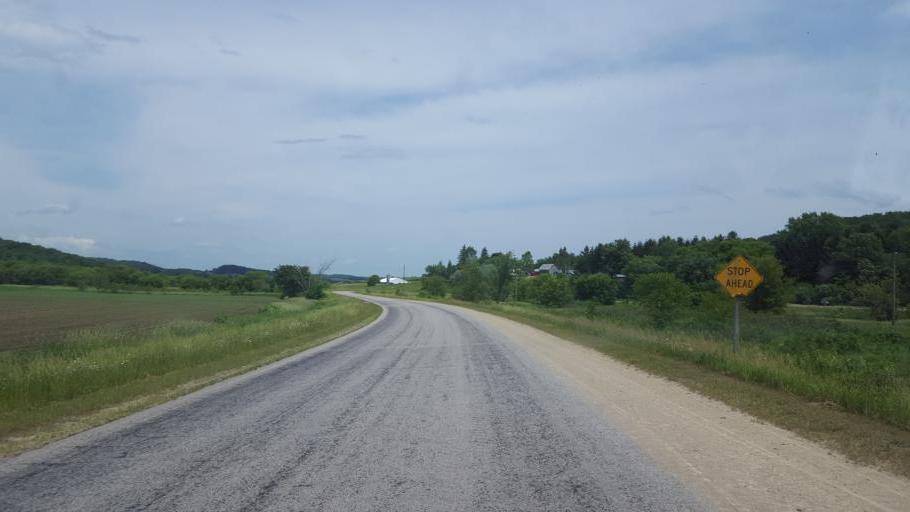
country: US
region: Wisconsin
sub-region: Vernon County
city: Hillsboro
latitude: 43.6149
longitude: -90.3573
